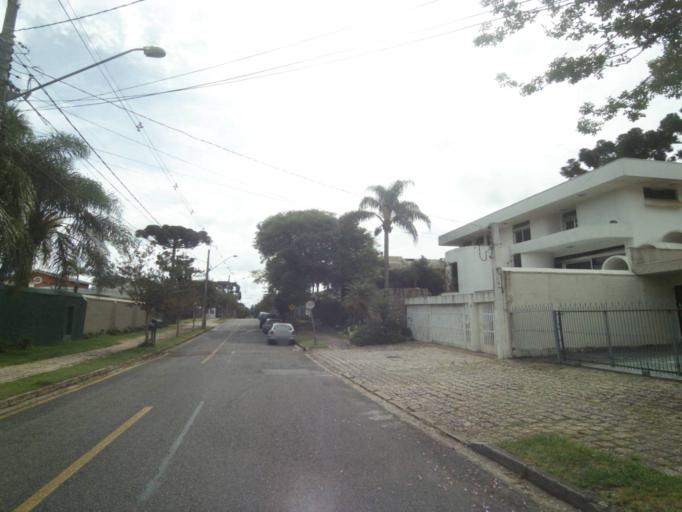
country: BR
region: Parana
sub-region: Curitiba
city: Curitiba
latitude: -25.4440
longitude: -49.2982
